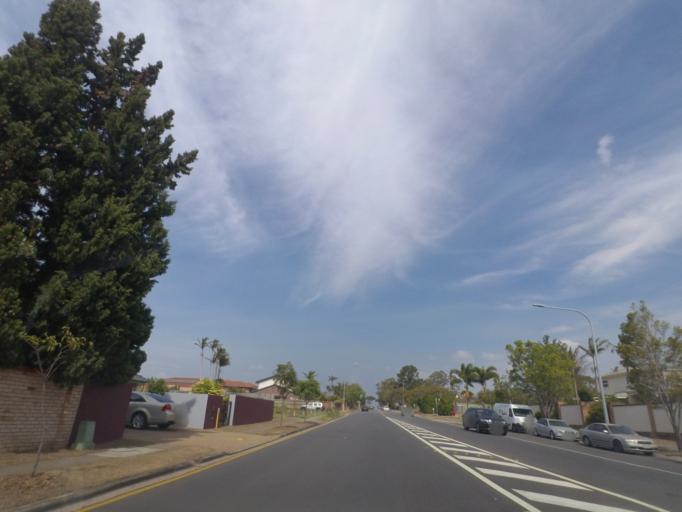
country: AU
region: Queensland
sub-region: Brisbane
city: Sunnybank Hills
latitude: -27.5989
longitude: 153.0546
